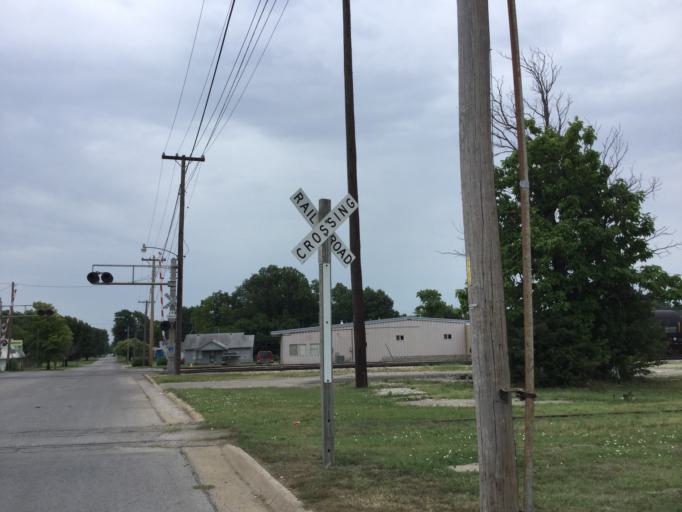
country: US
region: Kansas
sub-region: Montgomery County
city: Coffeyville
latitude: 37.0402
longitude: -95.6131
